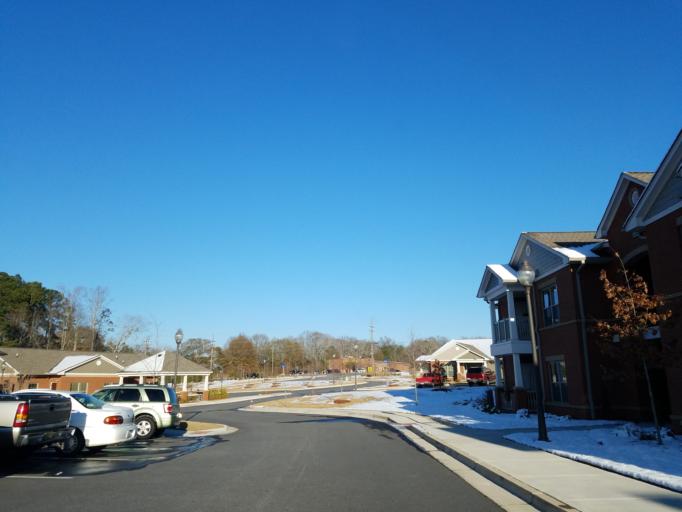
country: US
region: Georgia
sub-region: Dawson County
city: Dawsonville
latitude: 34.3574
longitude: -84.0341
